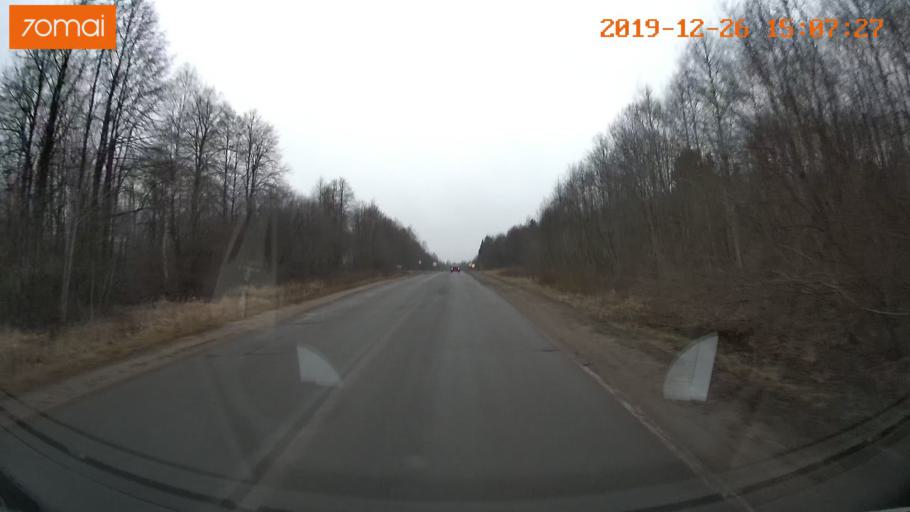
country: RU
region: Jaroslavl
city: Rybinsk
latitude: 58.1697
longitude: 38.8411
